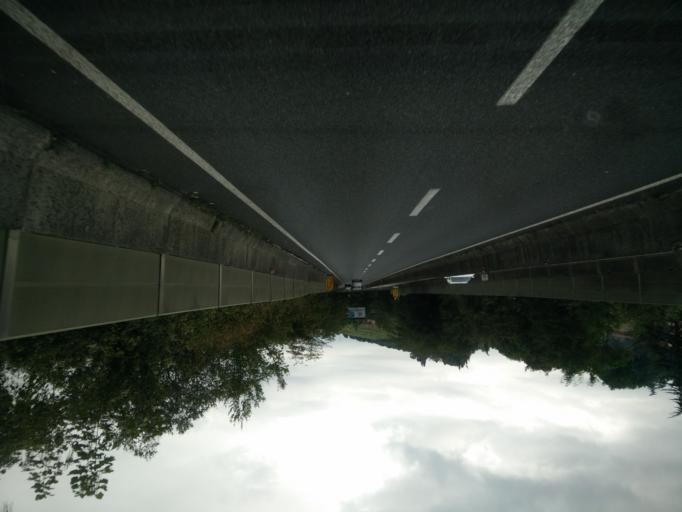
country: IT
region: Tuscany
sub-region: Province of Florence
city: Tavarnuzze
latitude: 43.7110
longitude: 11.2141
